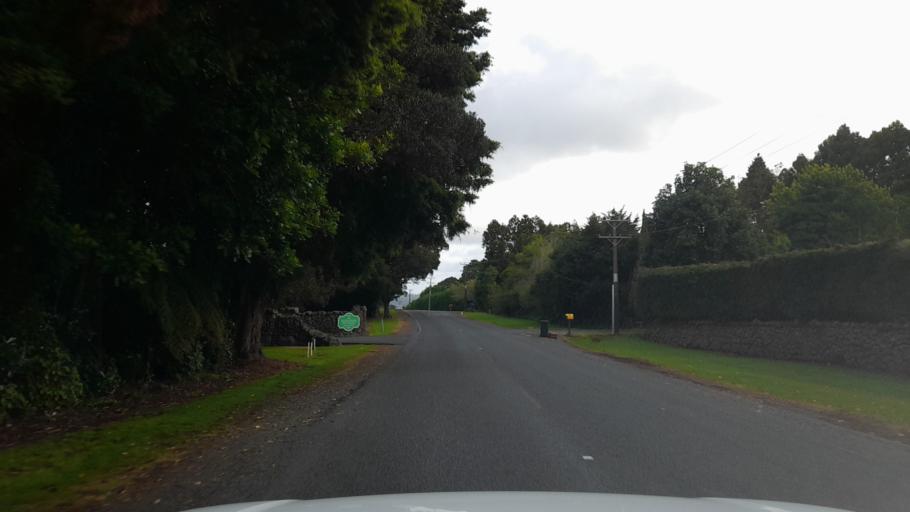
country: NZ
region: Northland
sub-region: Whangarei
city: Maungatapere
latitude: -35.7466
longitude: 174.2552
